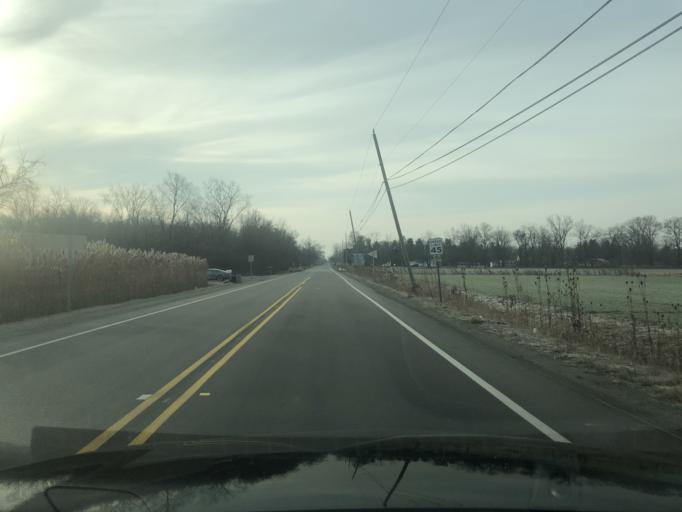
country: US
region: Michigan
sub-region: Wayne County
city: Taylor
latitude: 42.1798
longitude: -83.3255
